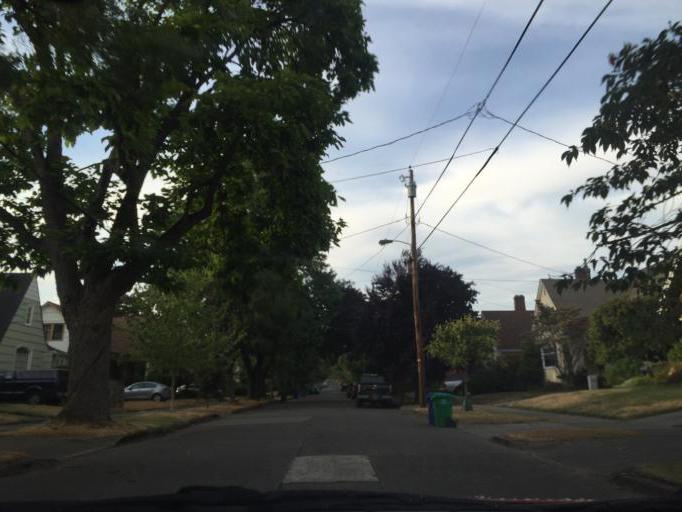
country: US
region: Oregon
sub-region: Multnomah County
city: Portland
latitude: 45.5436
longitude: -122.6327
